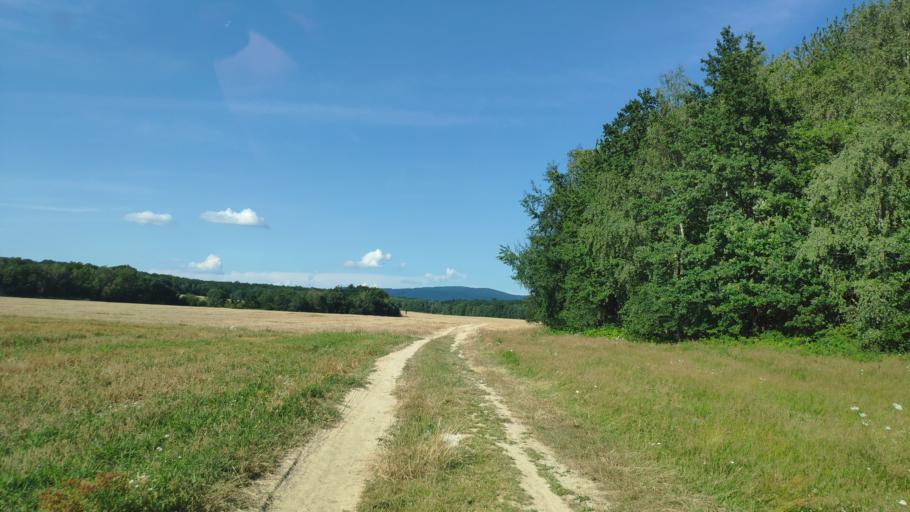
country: SK
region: Presovsky
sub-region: Okres Presov
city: Presov
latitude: 48.9124
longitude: 21.2961
